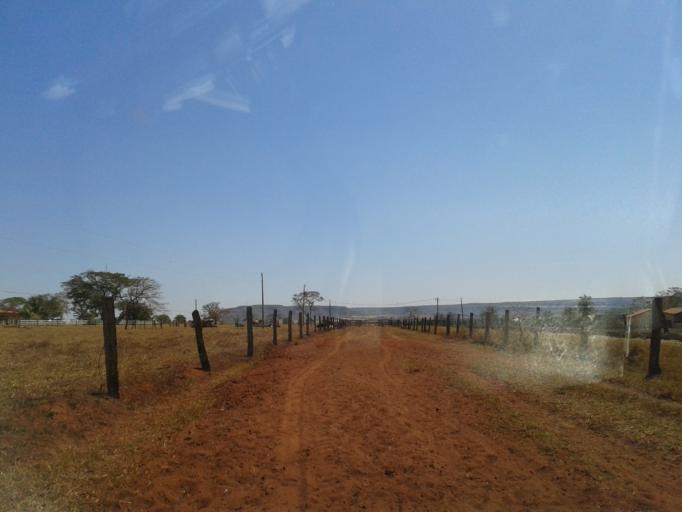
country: BR
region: Minas Gerais
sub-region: Santa Vitoria
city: Santa Vitoria
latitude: -19.0737
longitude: -50.0370
